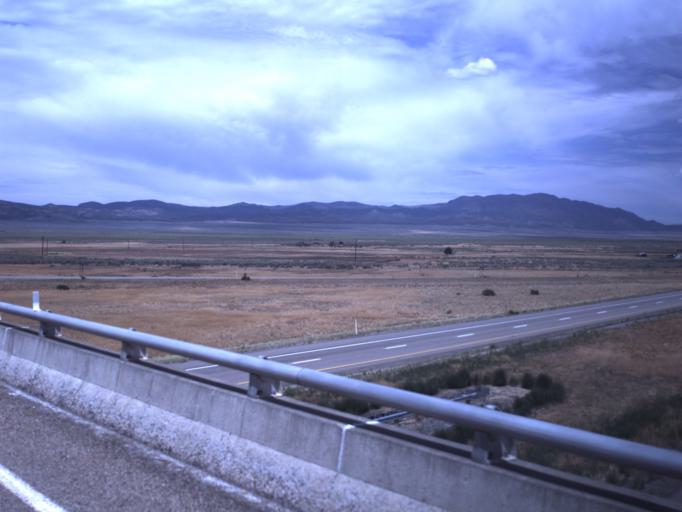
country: US
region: Utah
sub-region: Iron County
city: Parowan
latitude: 37.9088
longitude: -112.7770
